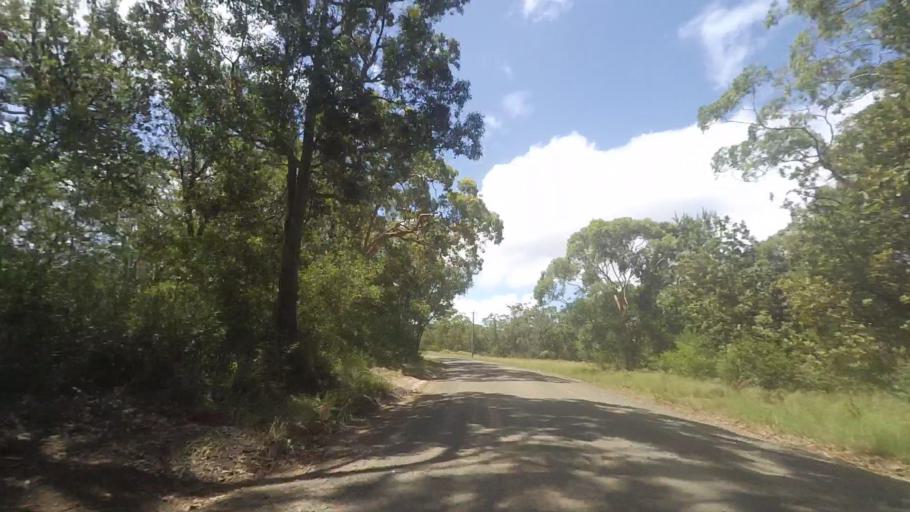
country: AU
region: New South Wales
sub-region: Great Lakes
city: Bulahdelah
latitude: -32.5078
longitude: 152.2925
